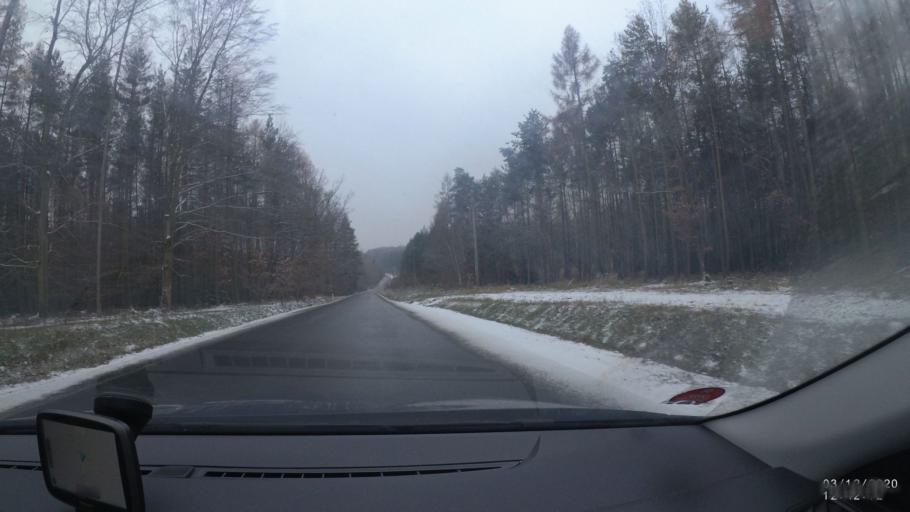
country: CZ
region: Central Bohemia
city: Revnicov
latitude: 50.1668
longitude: 13.8422
